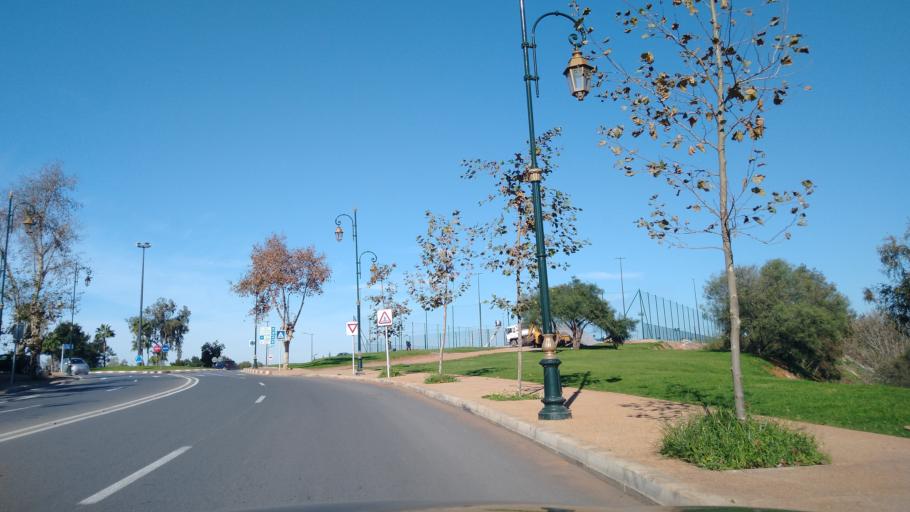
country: MA
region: Rabat-Sale-Zemmour-Zaer
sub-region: Rabat
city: Rabat
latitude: 33.9987
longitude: -6.8245
